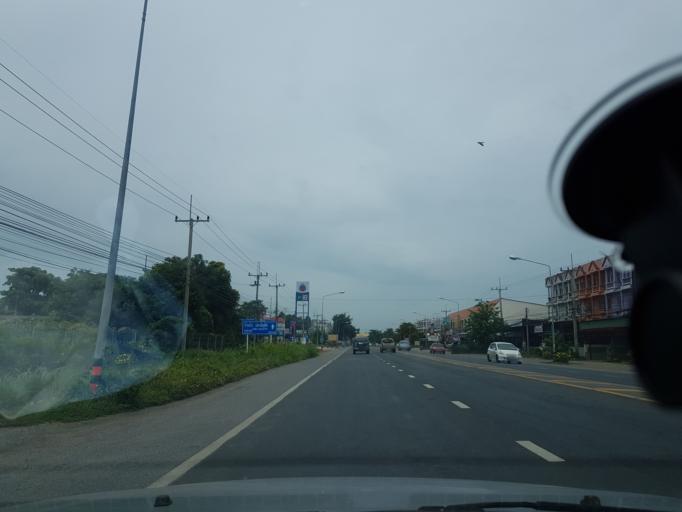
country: TH
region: Lop Buri
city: Lop Buri
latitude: 14.8090
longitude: 100.5989
